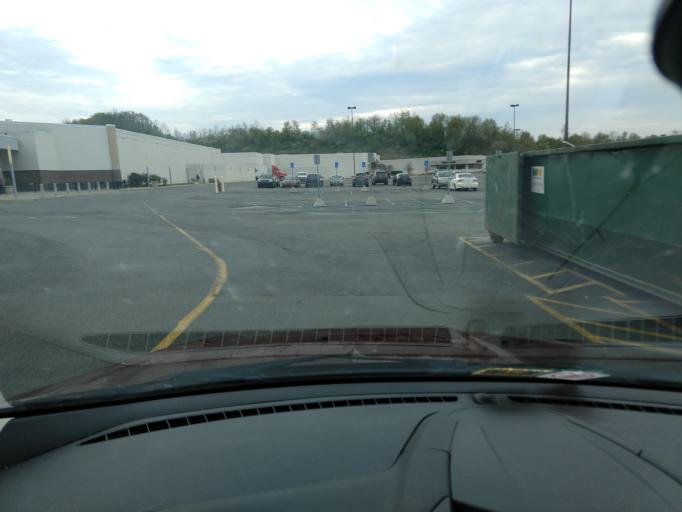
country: US
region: West Virginia
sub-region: Harrison County
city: Bridgeport
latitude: 39.3118
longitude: -80.2721
